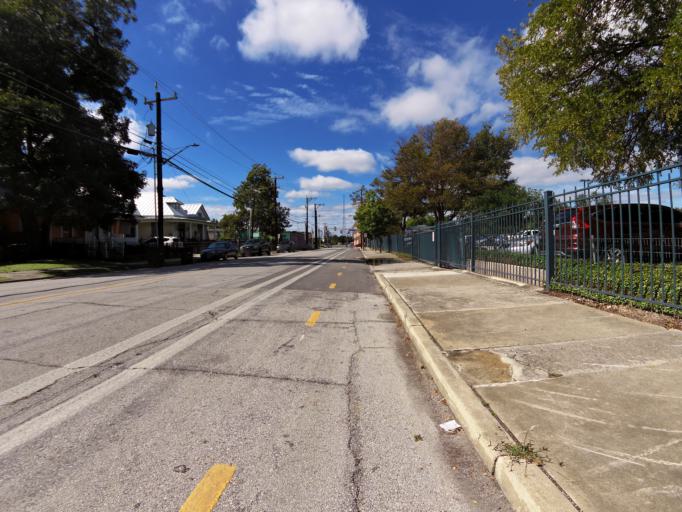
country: US
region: Texas
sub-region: Bexar County
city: San Antonio
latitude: 29.4168
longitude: -98.4968
